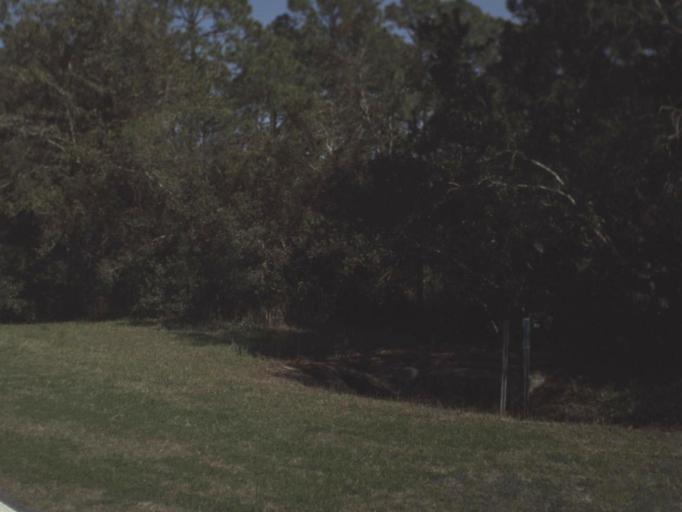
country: US
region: Florida
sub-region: Franklin County
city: Carrabelle
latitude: 29.8729
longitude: -84.6084
